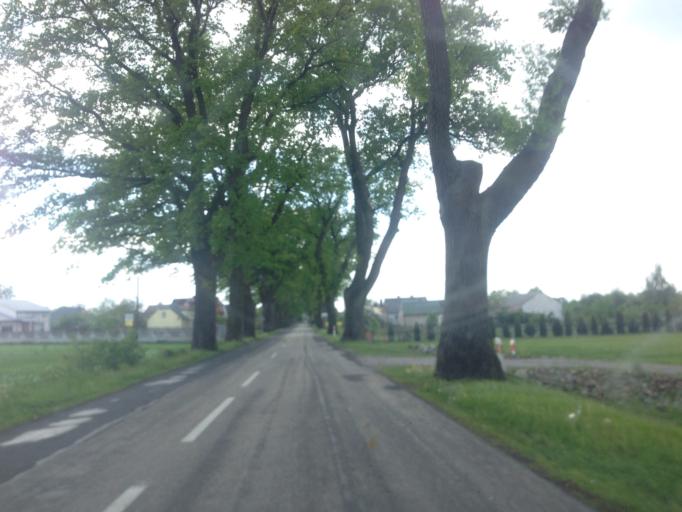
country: PL
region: Kujawsko-Pomorskie
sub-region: Powiat swiecki
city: Pruszcz
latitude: 53.2848
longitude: 18.1320
